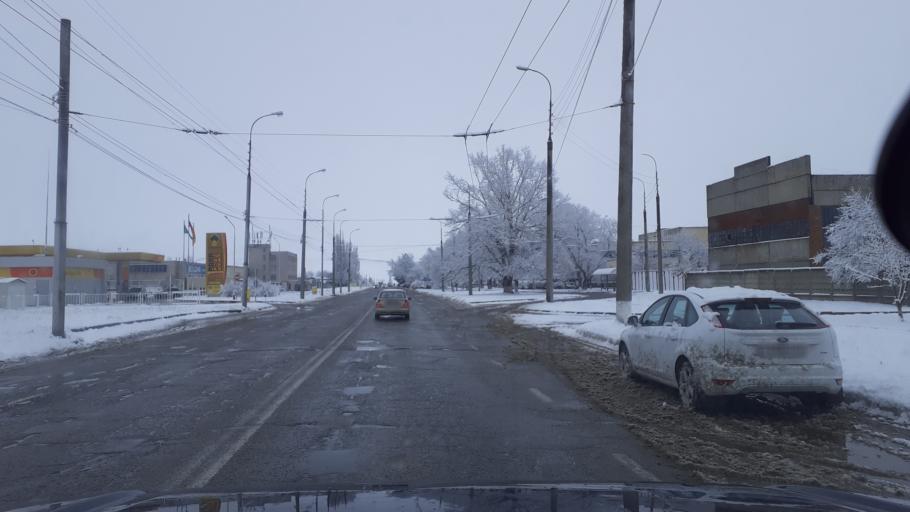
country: RU
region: Adygeya
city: Maykop
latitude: 44.6309
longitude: 40.1240
